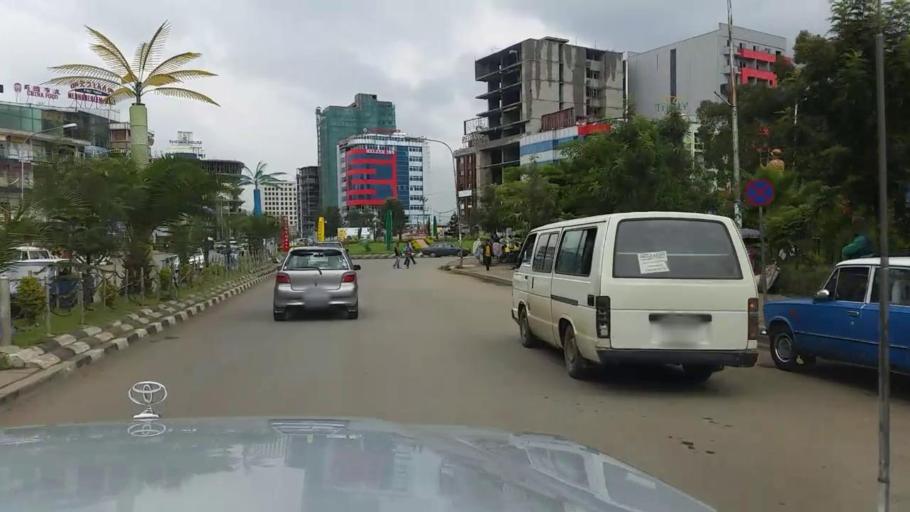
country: ET
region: Adis Abeba
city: Addis Ababa
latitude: 8.9973
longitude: 38.7872
